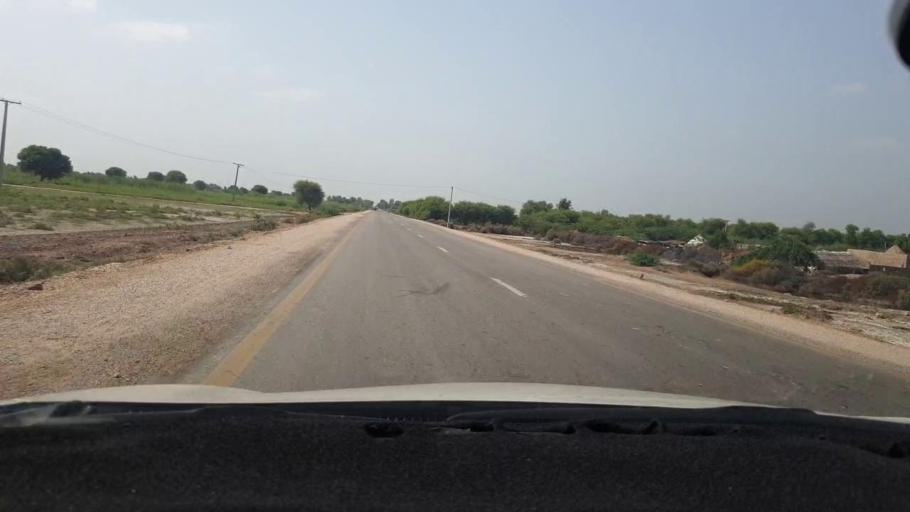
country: PK
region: Sindh
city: Mirpur Khas
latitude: 25.6487
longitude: 69.0979
